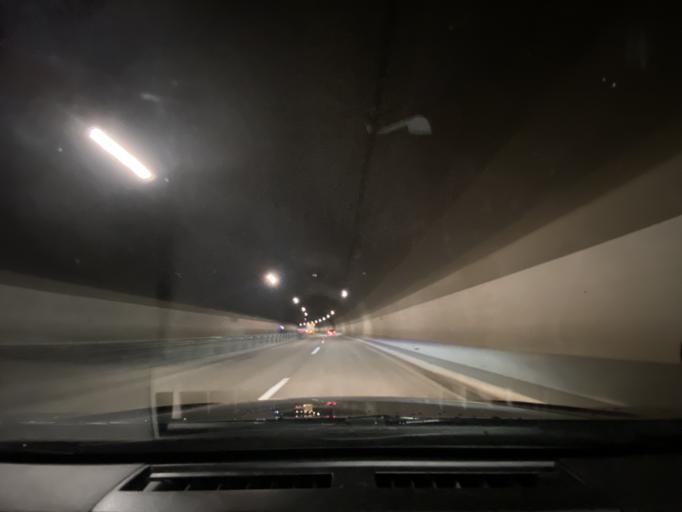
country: JP
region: Hokkaido
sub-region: Asahikawa-shi
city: Asahikawa
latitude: 43.7728
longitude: 142.3059
